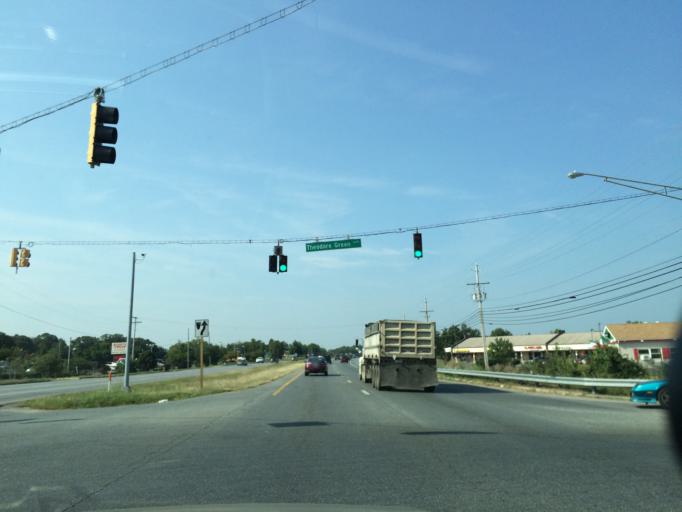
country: US
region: Maryland
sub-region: Charles County
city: Saint Charles
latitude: 38.5880
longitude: -76.9448
